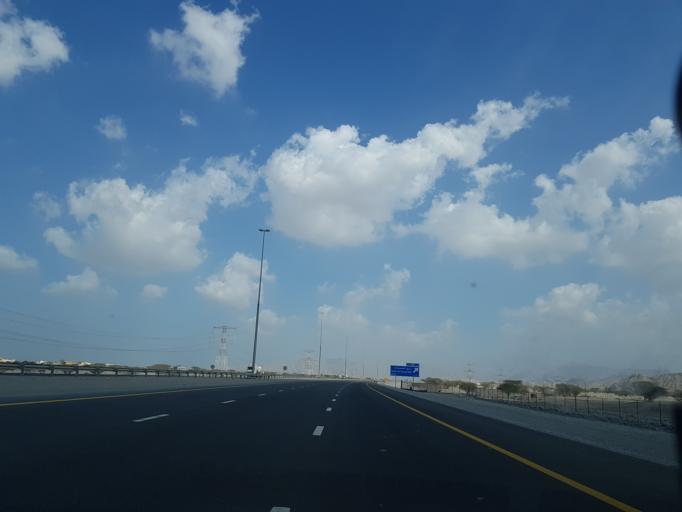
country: AE
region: Ra's al Khaymah
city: Ras al-Khaimah
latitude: 25.7536
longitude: 56.0179
